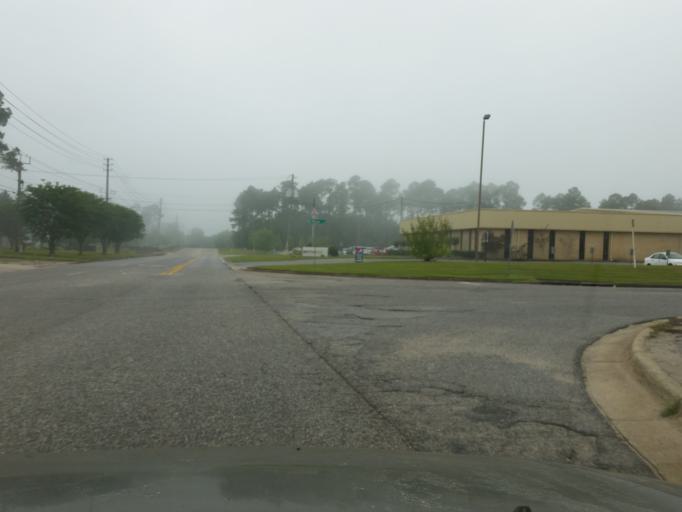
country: US
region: Florida
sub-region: Escambia County
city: Ferry Pass
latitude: 30.5236
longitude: -87.1900
